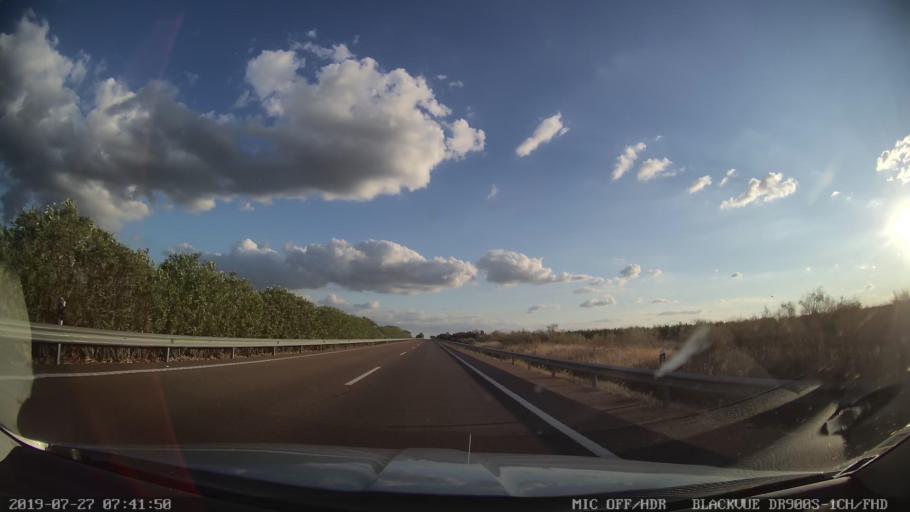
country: ES
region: Extremadura
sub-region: Provincia de Badajoz
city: Santa Amalia
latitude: 39.0234
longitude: -6.0793
